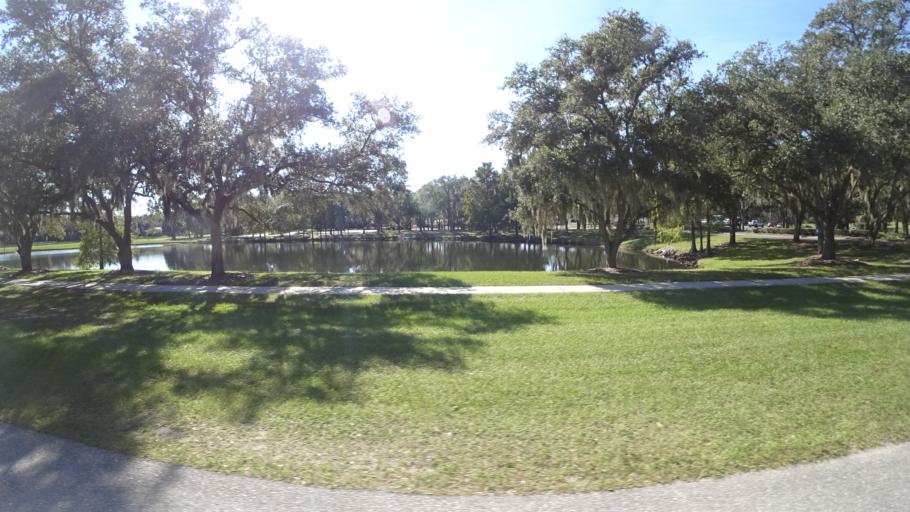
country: US
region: Florida
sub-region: Sarasota County
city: The Meadows
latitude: 27.4231
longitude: -82.4329
